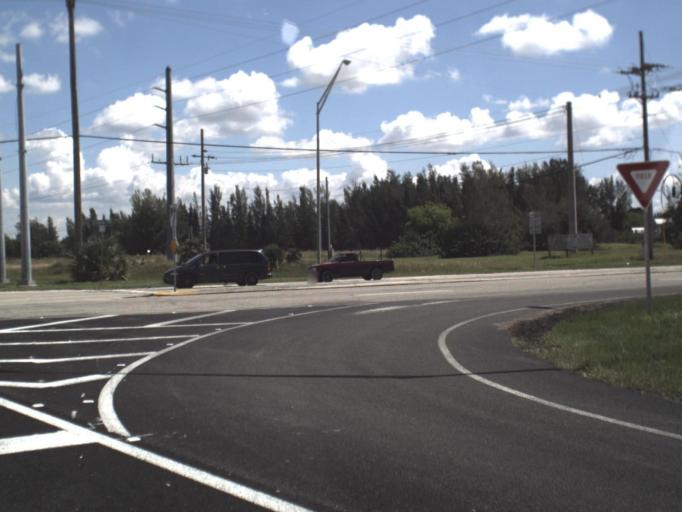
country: US
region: Florida
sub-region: Lee County
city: Cape Coral
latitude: 26.6384
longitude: -82.0075
